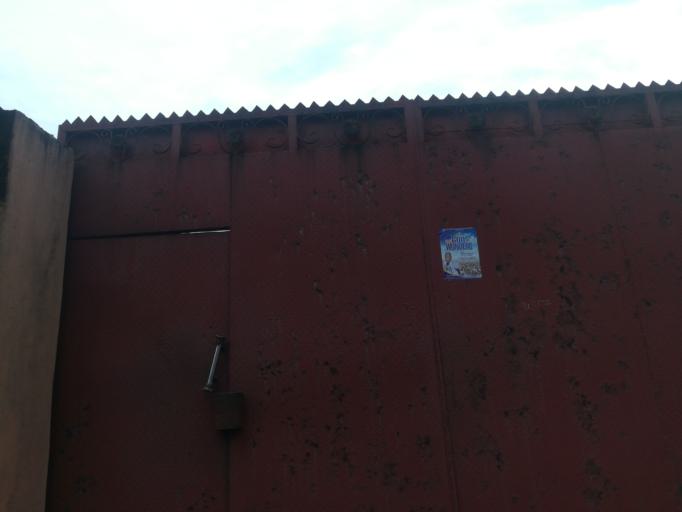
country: NG
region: Rivers
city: Port Harcourt
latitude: 4.7947
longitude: 6.9599
